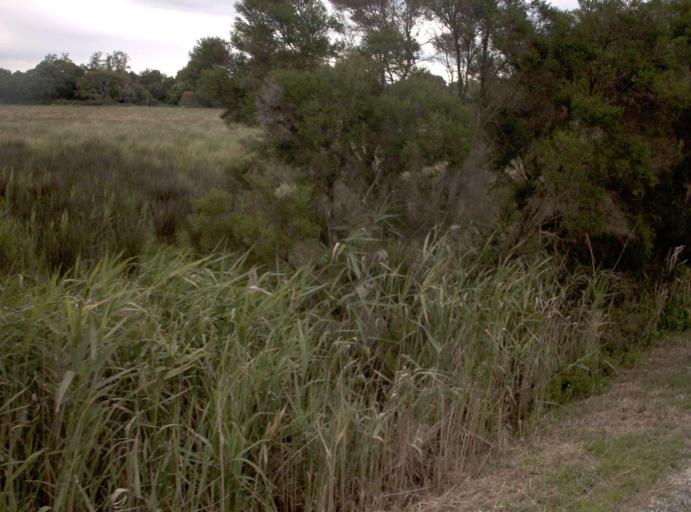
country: AU
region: Victoria
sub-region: Wellington
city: Sale
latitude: -38.0256
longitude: 147.1793
